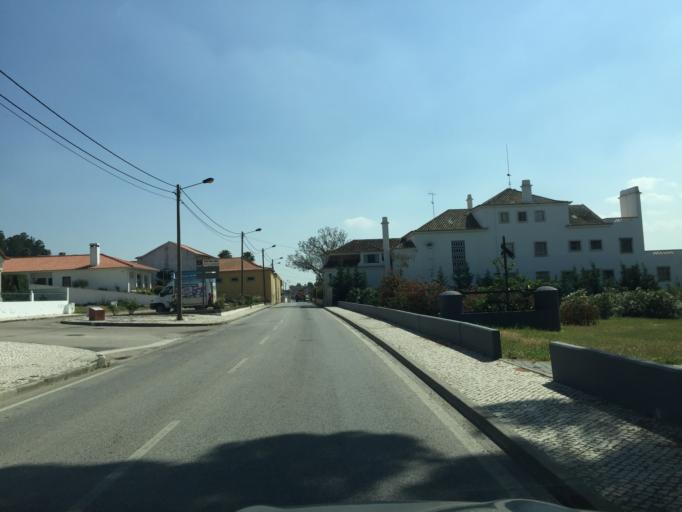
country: PT
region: Santarem
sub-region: Golega
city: Golega
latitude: 39.3644
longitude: -8.4773
